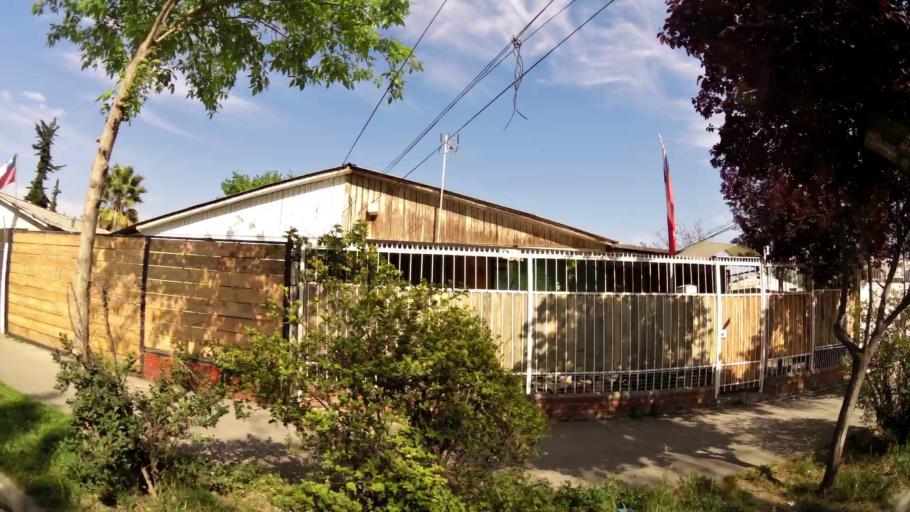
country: CL
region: Santiago Metropolitan
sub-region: Provincia de Santiago
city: La Pintana
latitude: -33.5561
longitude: -70.5983
